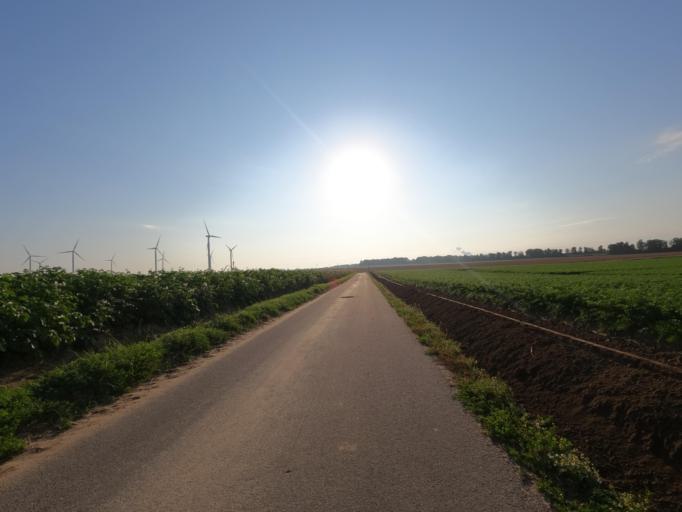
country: DE
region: North Rhine-Westphalia
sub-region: Regierungsbezirk Koln
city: Titz
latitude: 51.0153
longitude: 6.4081
